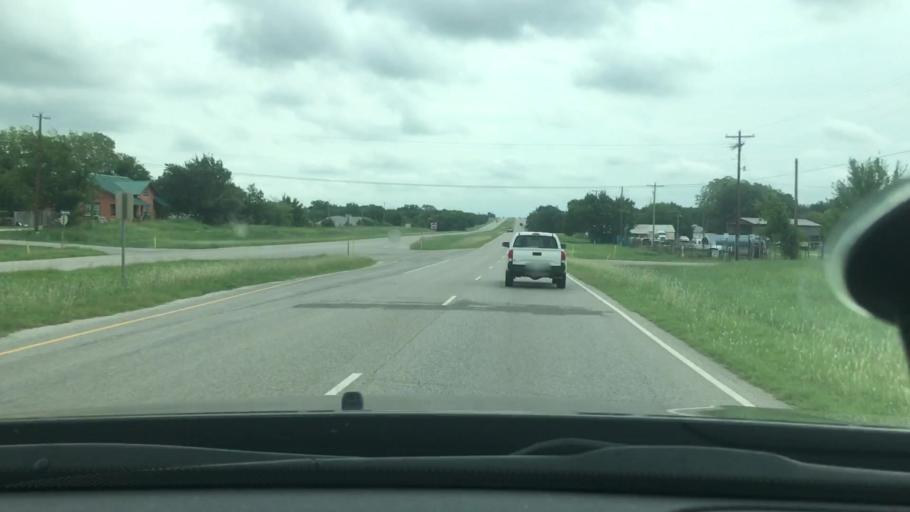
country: US
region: Oklahoma
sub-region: Carter County
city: Wilson
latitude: 34.1728
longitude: -97.4579
